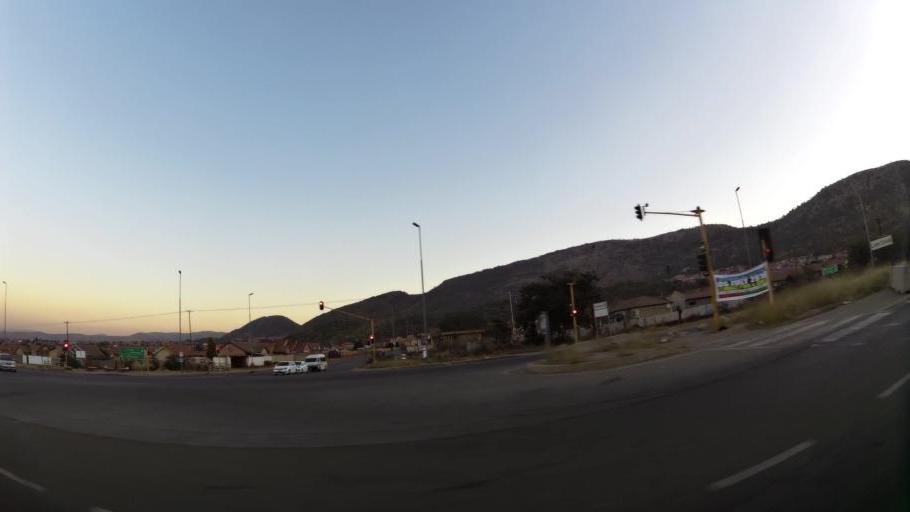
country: ZA
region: North-West
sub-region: Bojanala Platinum District Municipality
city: Rustenburg
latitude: -25.6400
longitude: 27.1997
